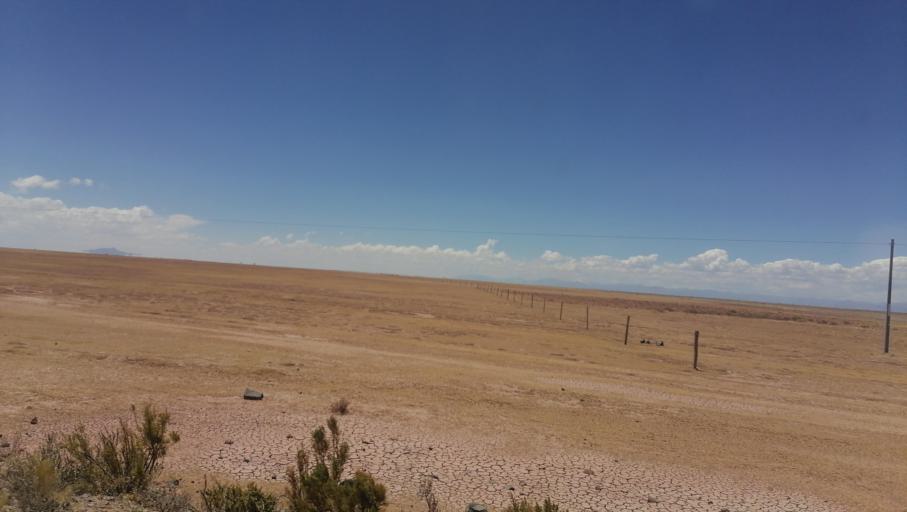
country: BO
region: Oruro
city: Challapata
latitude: -19.2242
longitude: -66.9695
